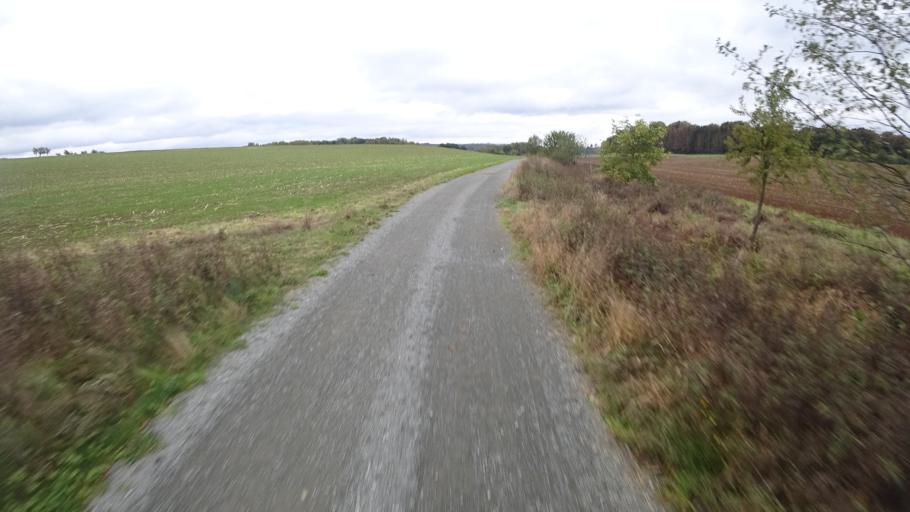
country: DE
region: Rheinland-Pfalz
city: Maxsain
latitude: 50.5574
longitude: 7.7794
